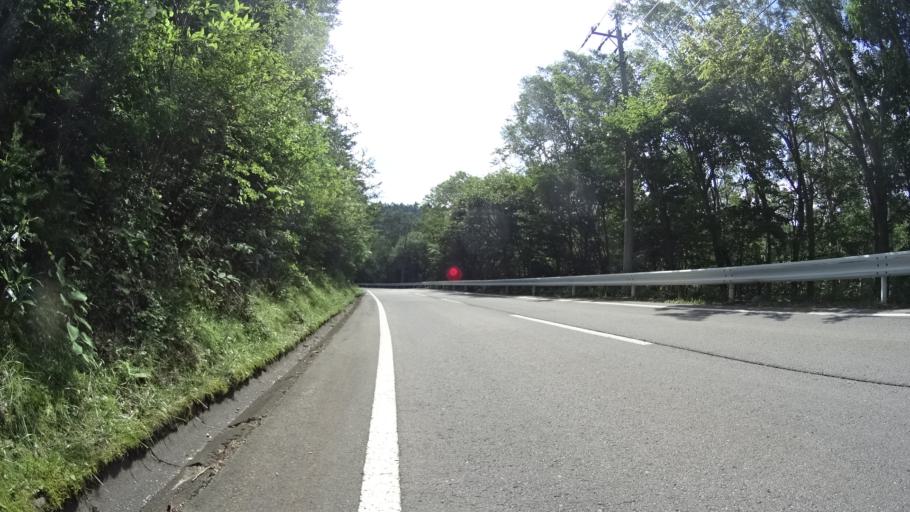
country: JP
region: Nagano
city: Saku
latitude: 36.0538
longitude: 138.4025
